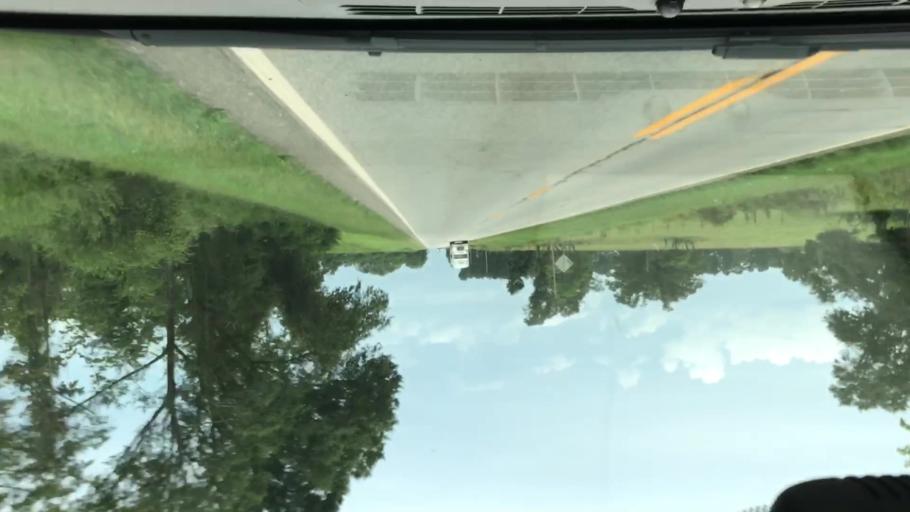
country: US
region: Georgia
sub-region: Early County
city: Blakely
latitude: 31.3292
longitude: -85.0040
